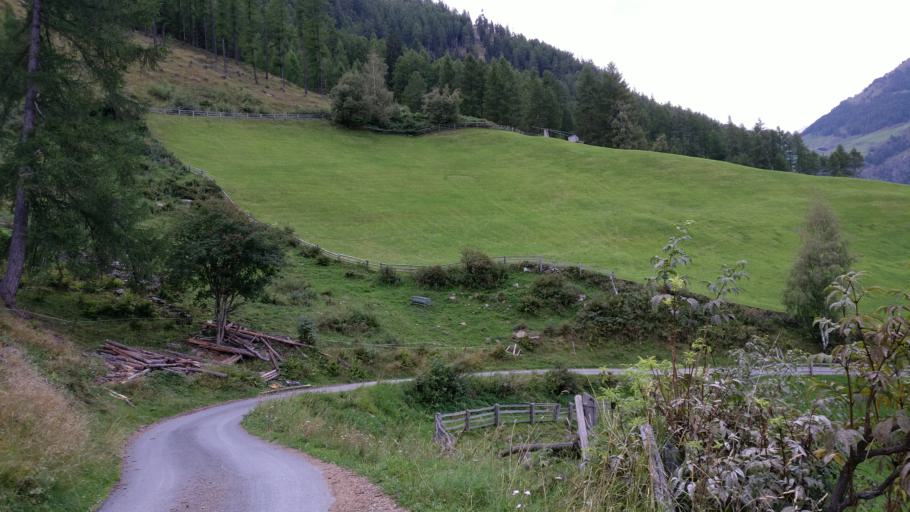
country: IT
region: Trentino-Alto Adige
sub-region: Bolzano
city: Certosa
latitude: 46.7018
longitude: 10.9075
